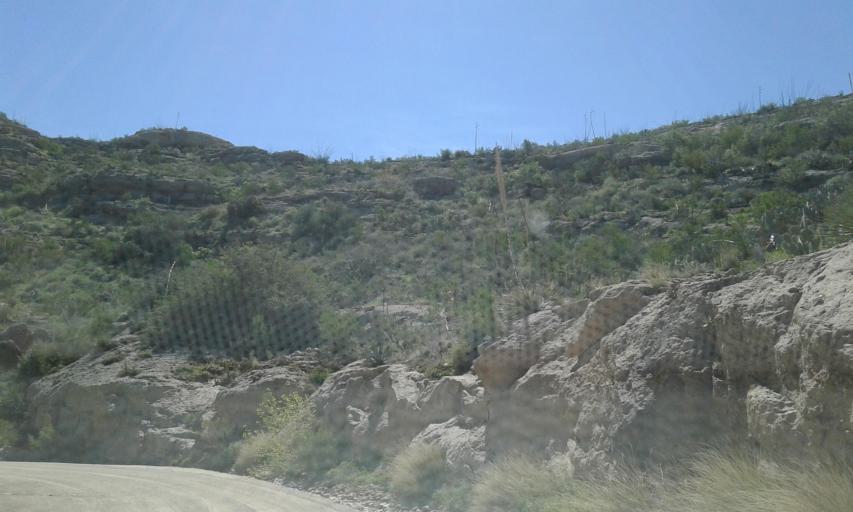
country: US
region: Arizona
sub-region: Pinal County
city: Gold Camp
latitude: 33.5345
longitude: -111.3112
